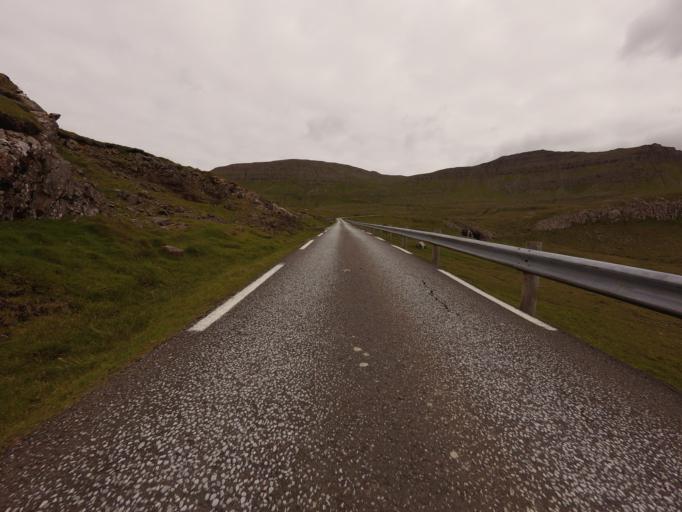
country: FO
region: Suduroy
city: Tvoroyri
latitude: 61.5189
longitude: -6.8546
